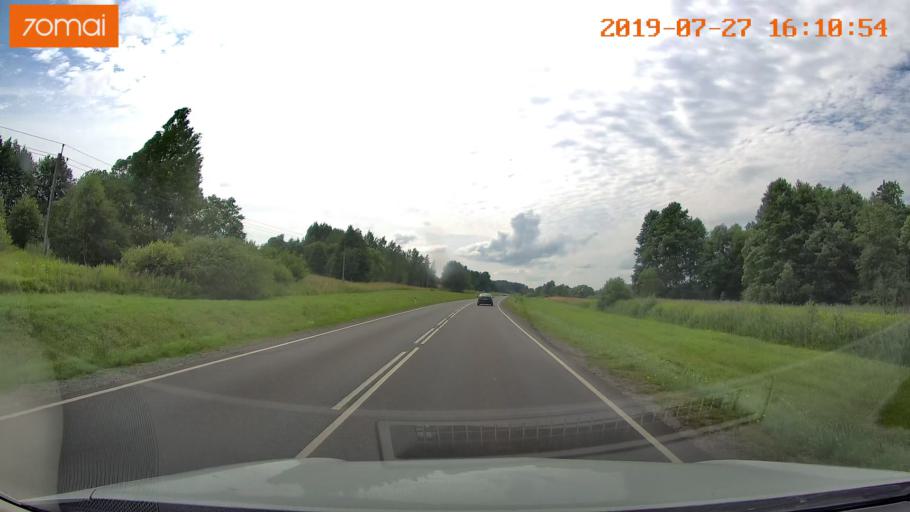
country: RU
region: Kaliningrad
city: Chernyakhovsk
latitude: 54.6343
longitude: 21.6866
